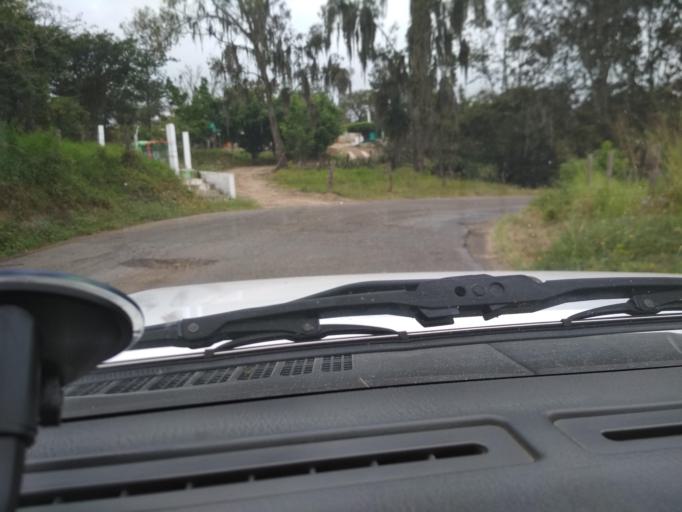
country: MX
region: Veracruz
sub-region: Emiliano Zapata
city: Dos Rios
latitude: 19.5344
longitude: -96.8015
